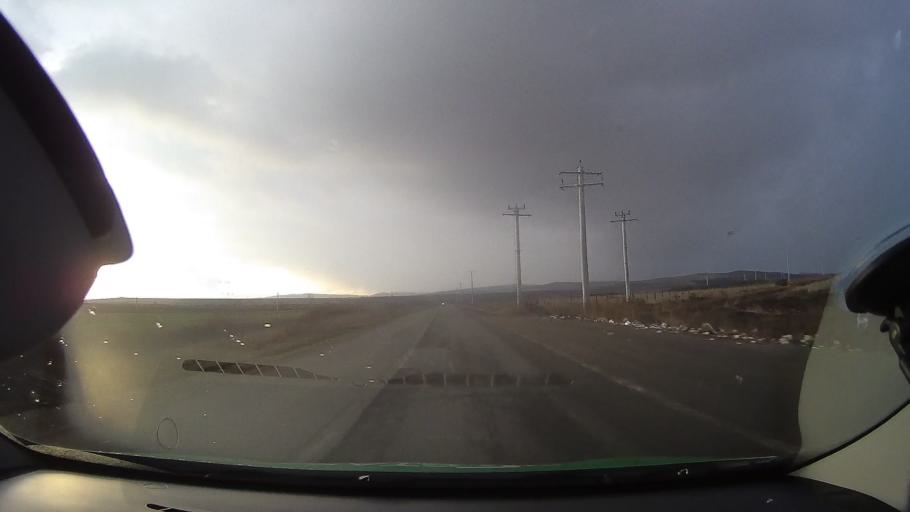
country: RO
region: Alba
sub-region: Comuna Lunca Muresului
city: Lunca Muresului
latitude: 46.4494
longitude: 23.9238
